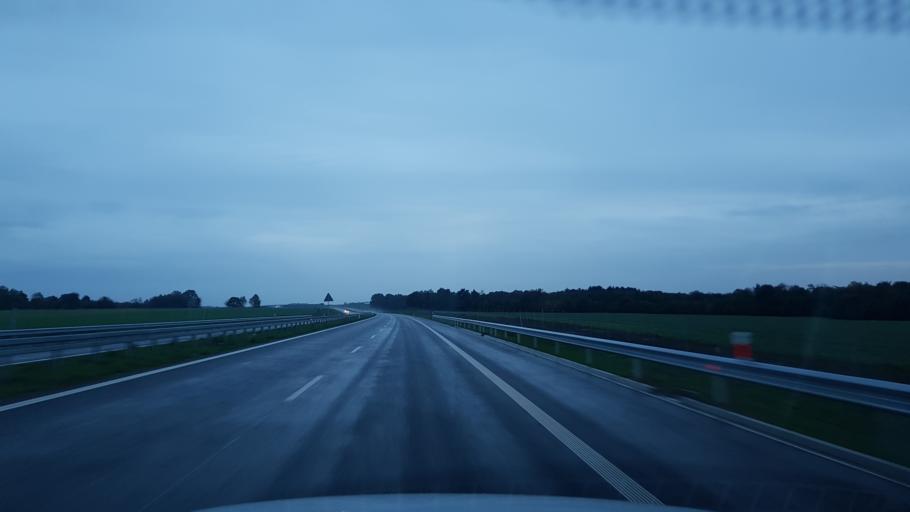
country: PL
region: West Pomeranian Voivodeship
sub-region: Powiat gryficki
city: Brojce
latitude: 53.9599
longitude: 15.4192
